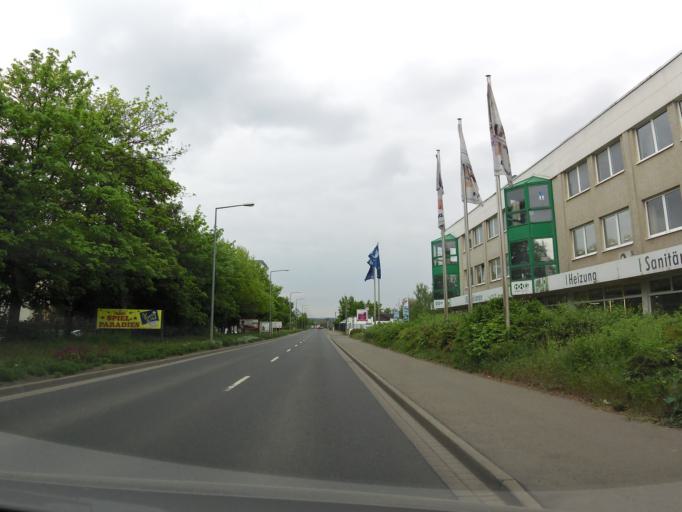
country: DE
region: Thuringia
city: Gotha
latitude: 50.9598
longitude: 10.7257
